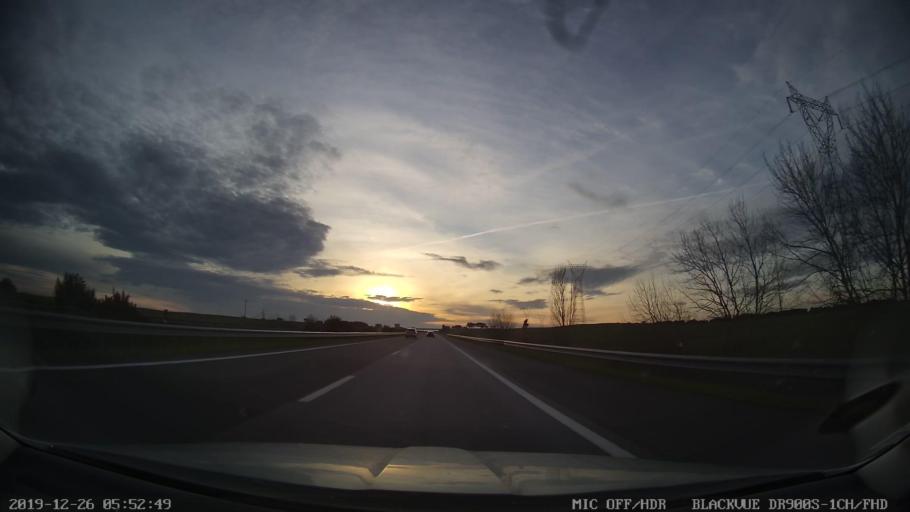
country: PT
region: Evora
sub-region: Evora
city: Evora
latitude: 38.6428
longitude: -7.8650
